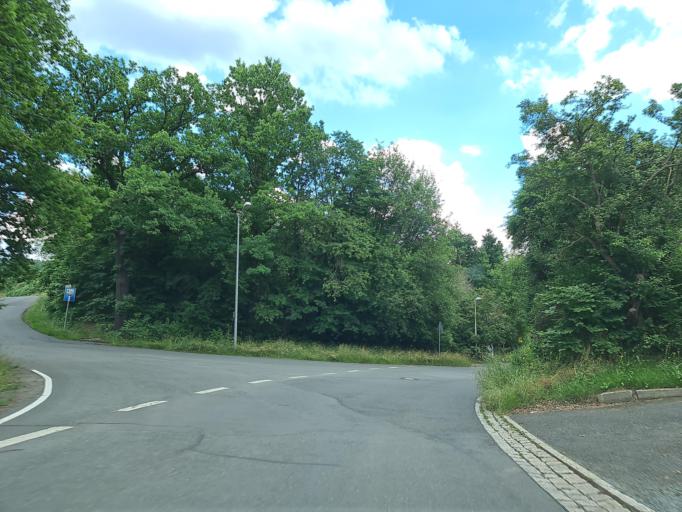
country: DE
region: Saxony
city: Plauen
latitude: 50.5144
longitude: 12.1609
